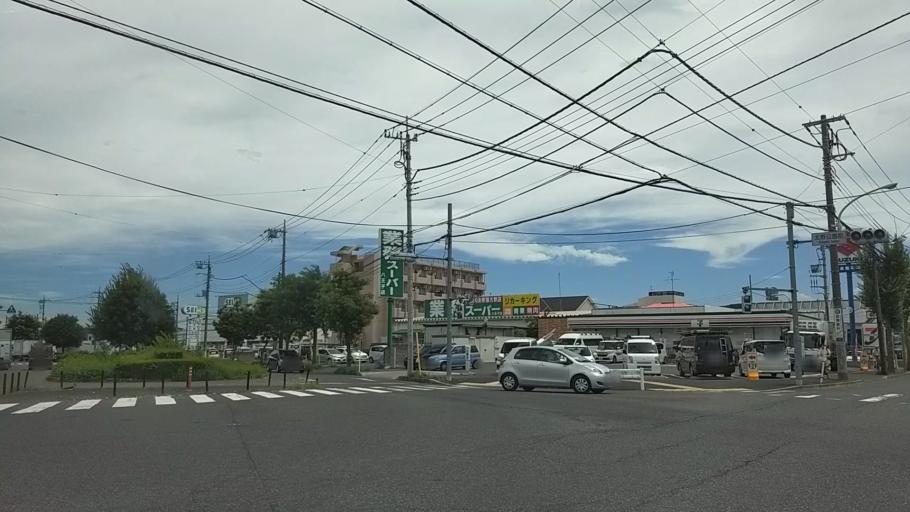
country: JP
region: Tokyo
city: Hachioji
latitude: 35.6482
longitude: 139.3590
